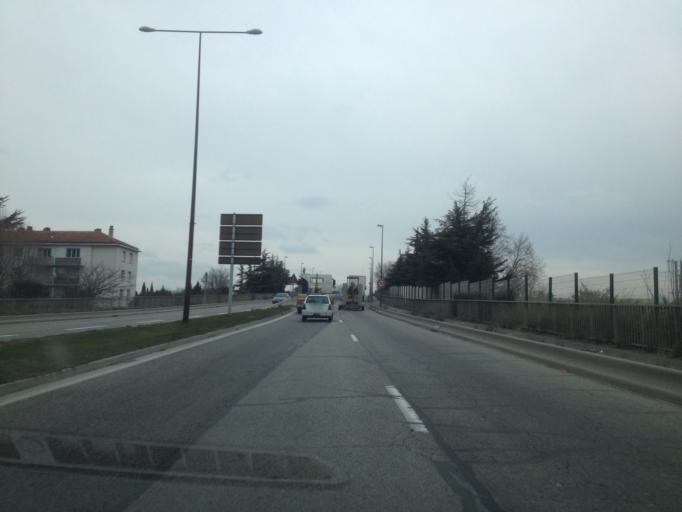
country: FR
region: Provence-Alpes-Cote d'Azur
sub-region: Departement du Vaucluse
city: Avignon
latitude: 43.9356
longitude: 4.8322
